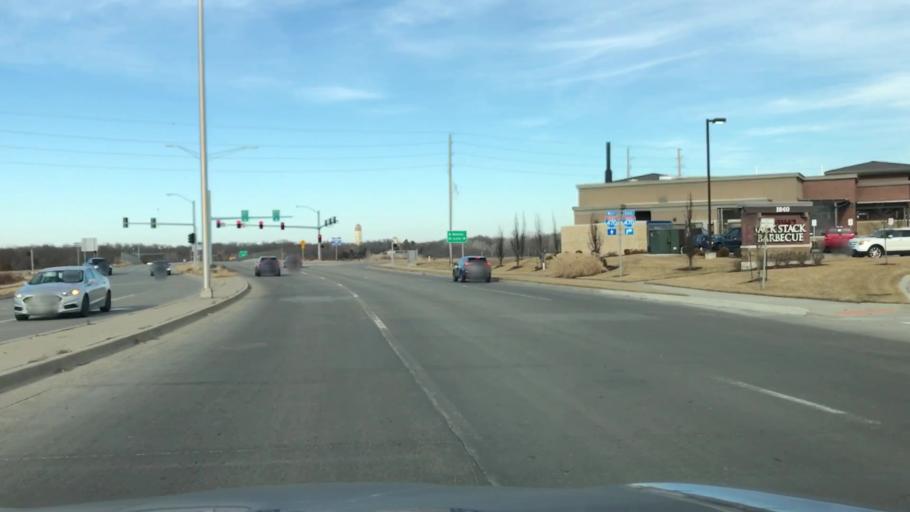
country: US
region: Missouri
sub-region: Jackson County
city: Lees Summit
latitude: 38.9317
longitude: -94.4123
